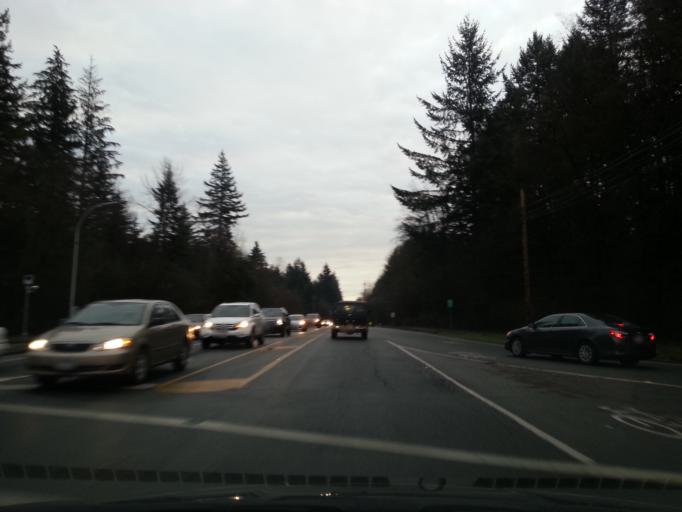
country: CA
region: British Columbia
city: Surrey
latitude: 49.1764
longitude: -122.8284
